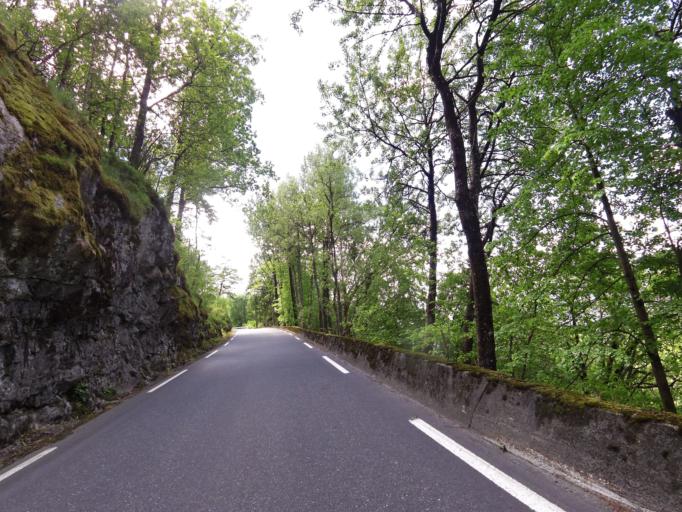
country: NO
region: Vest-Agder
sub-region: Kvinesdal
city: Liknes
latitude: 58.2913
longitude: 6.9404
